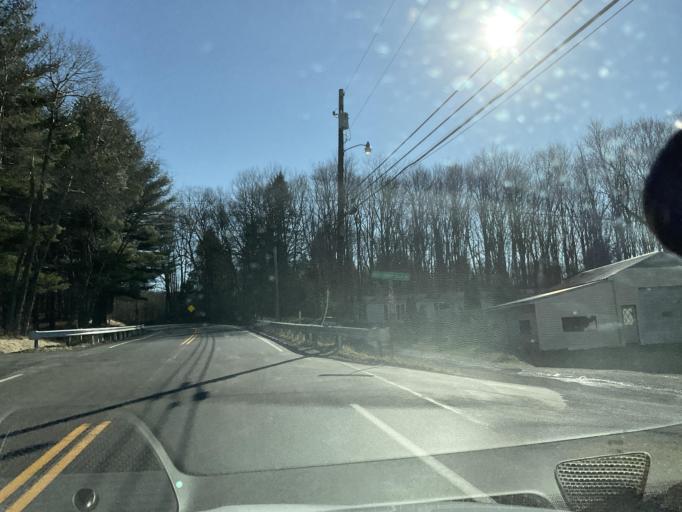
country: US
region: Maryland
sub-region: Garrett County
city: Oakland
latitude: 39.3889
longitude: -79.4596
